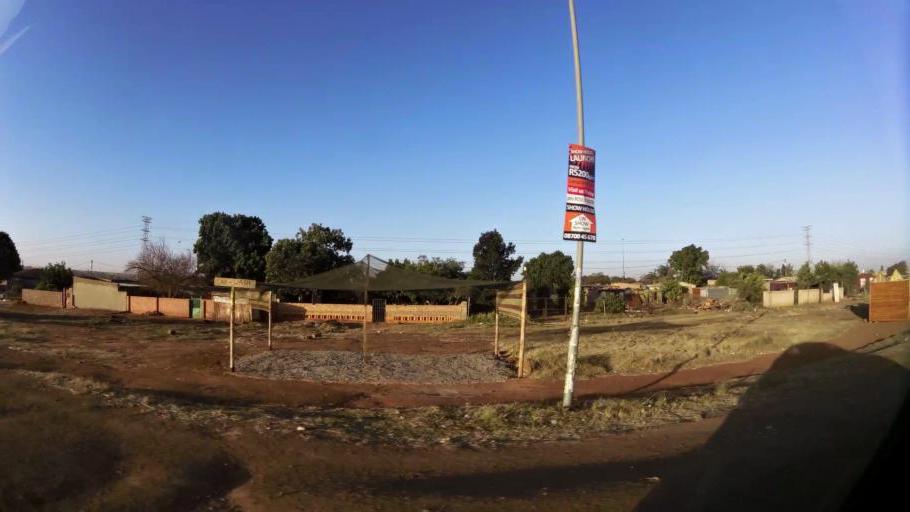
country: ZA
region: North-West
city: Ga-Rankuwa
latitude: -25.5915
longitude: 28.0762
